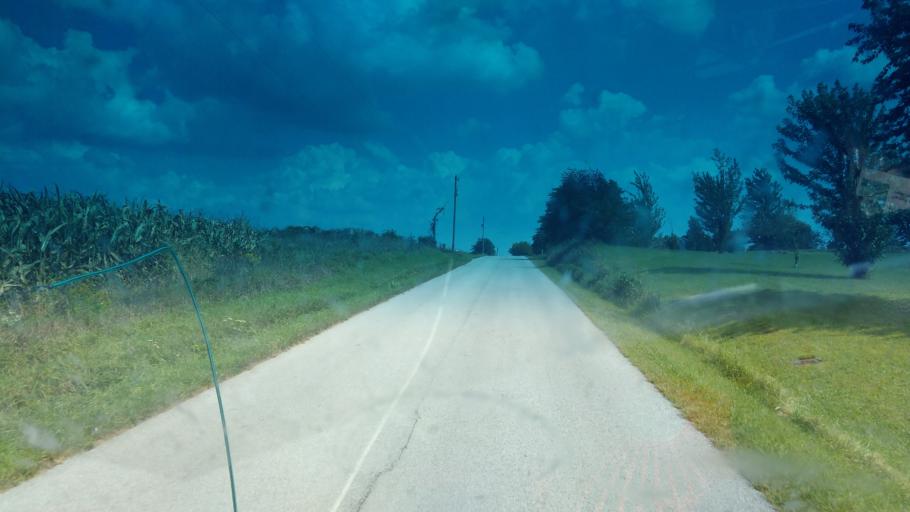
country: US
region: Ohio
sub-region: Hardin County
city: Ada
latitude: 40.7173
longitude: -83.9210
